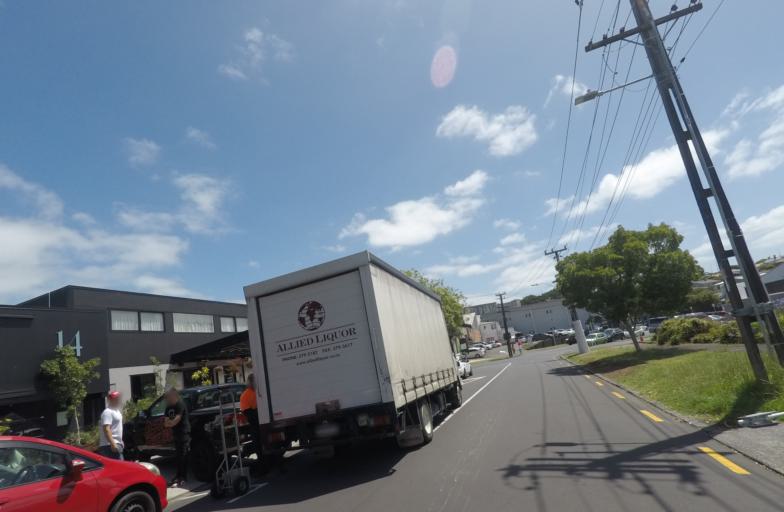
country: NZ
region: Auckland
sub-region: Auckland
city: Auckland
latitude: -36.8758
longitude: 174.7372
